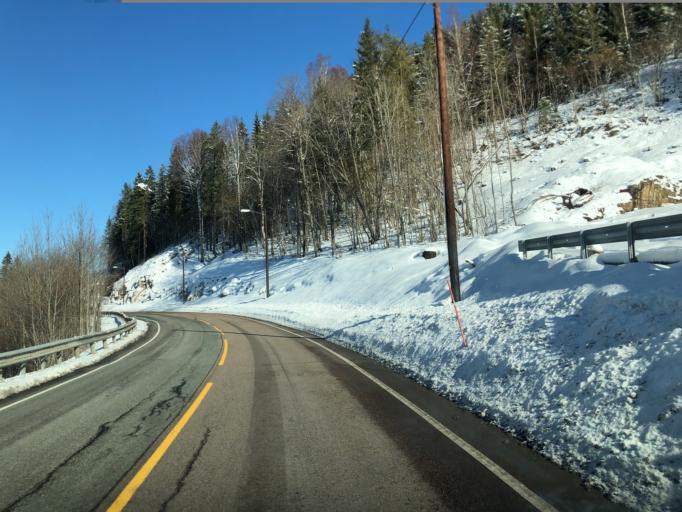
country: NO
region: Buskerud
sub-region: Lier
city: Tranby
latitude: 59.8402
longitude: 10.2651
